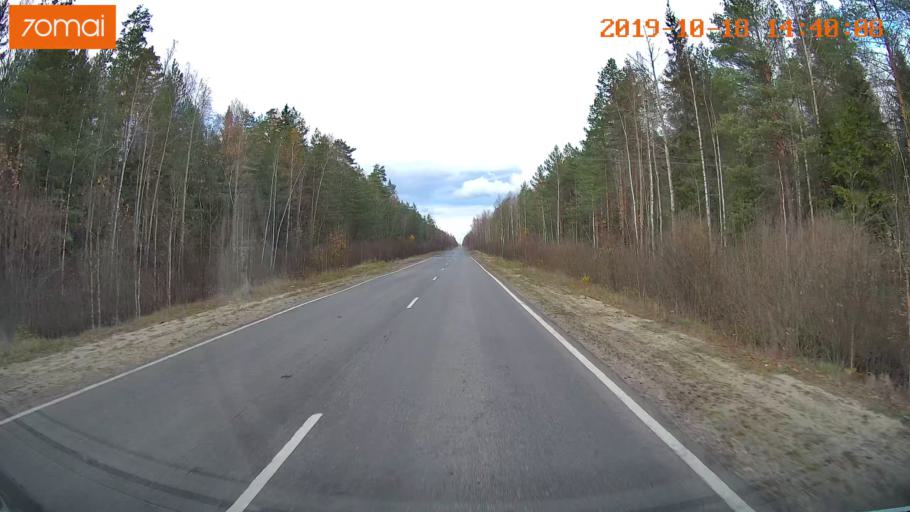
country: RU
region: Vladimir
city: Velikodvorskiy
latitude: 55.2721
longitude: 40.6684
